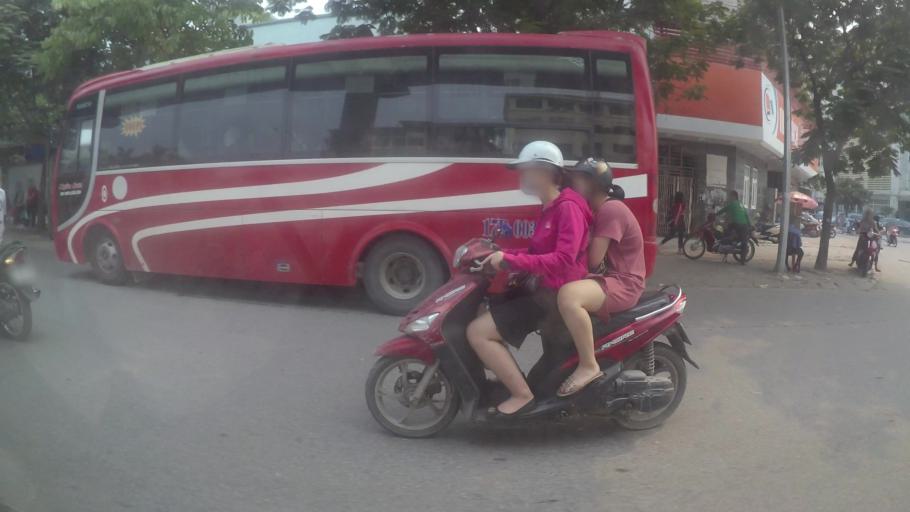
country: VN
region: Ha Noi
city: Cau Dien
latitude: 21.0375
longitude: 105.7740
